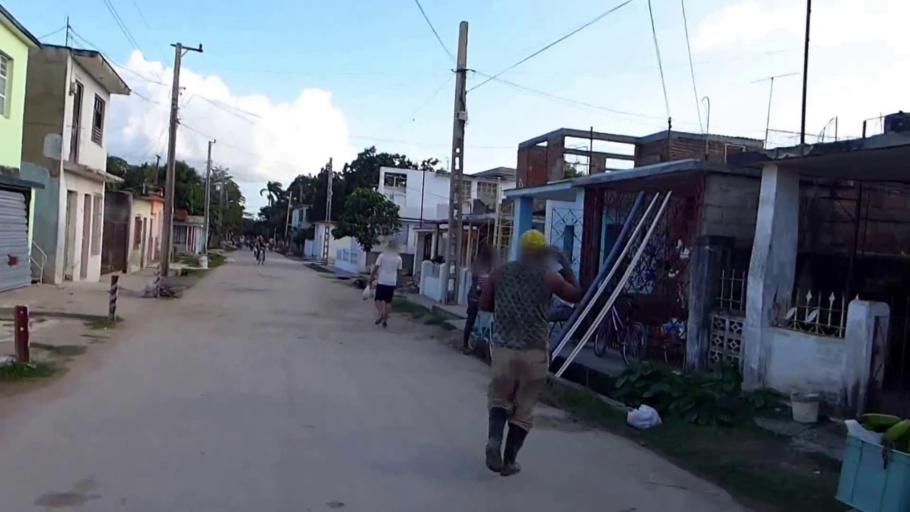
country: CU
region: Camaguey
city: Camaguey
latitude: 21.3968
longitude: -77.9046
